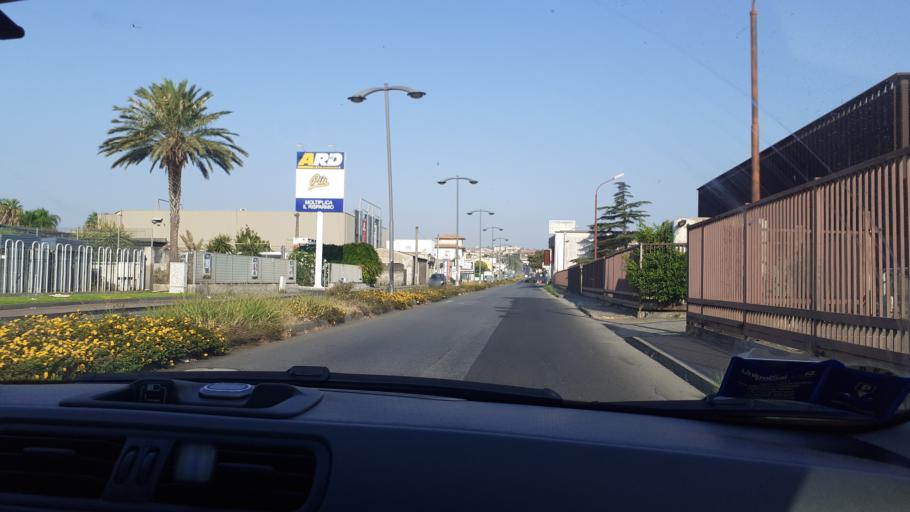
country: IT
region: Sicily
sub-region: Catania
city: Misterbianco
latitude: 37.5130
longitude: 15.0290
